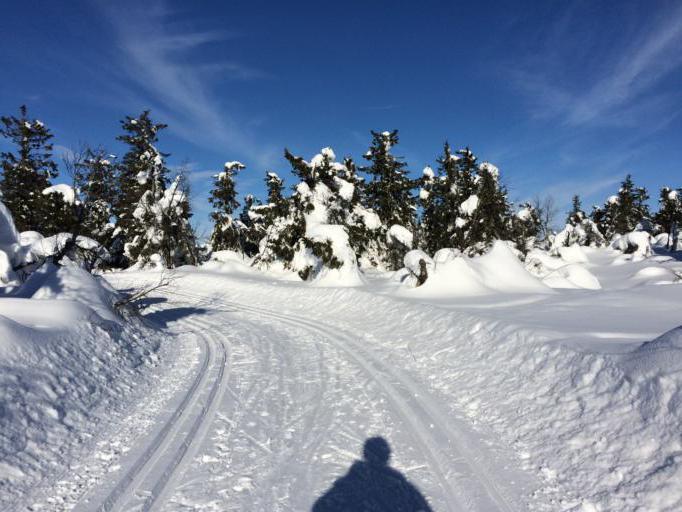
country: NO
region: Oppland
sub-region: Gausdal
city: Segalstad bru
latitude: 61.3099
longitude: 10.1044
